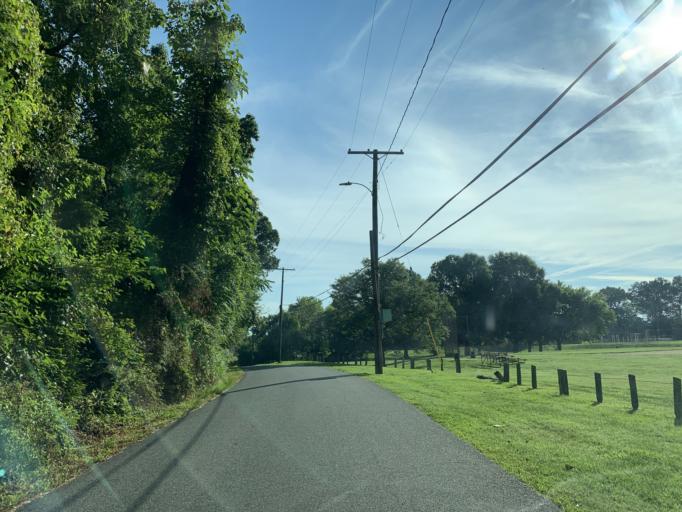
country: US
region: Maryland
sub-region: Baltimore County
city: Essex
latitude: 39.2931
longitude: -76.4592
